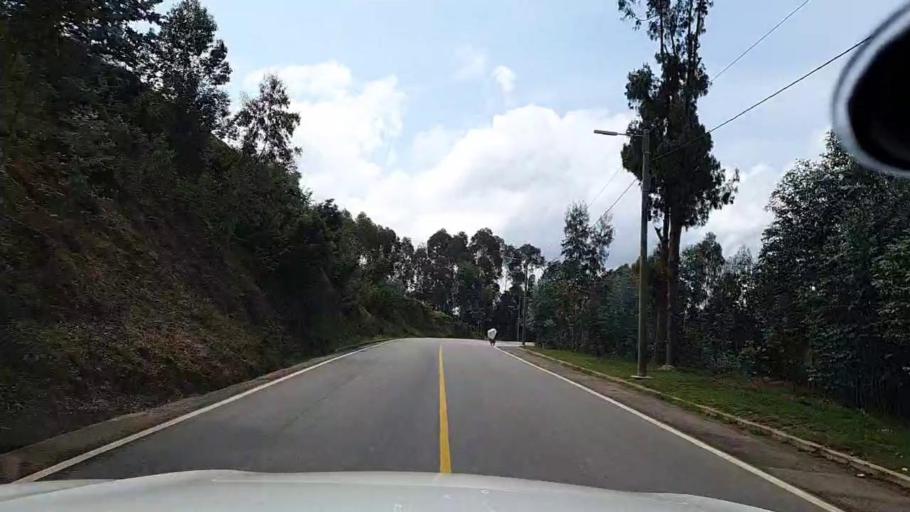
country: RW
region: Southern Province
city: Nzega
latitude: -2.5268
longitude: 29.4511
